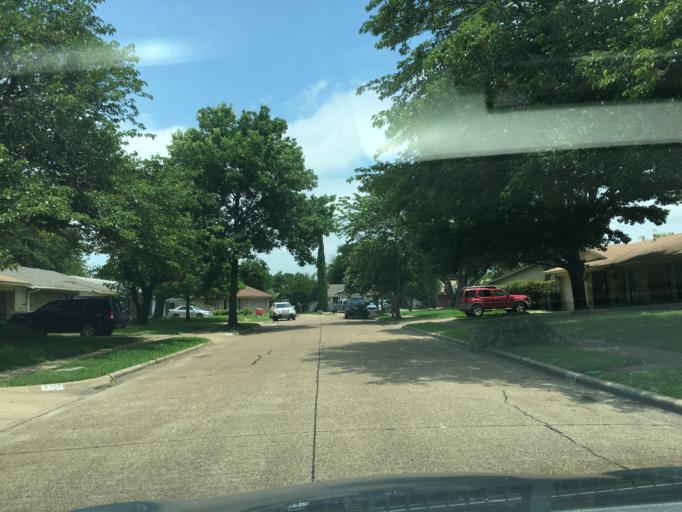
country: US
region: Texas
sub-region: Dallas County
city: Garland
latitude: 32.9195
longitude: -96.6811
